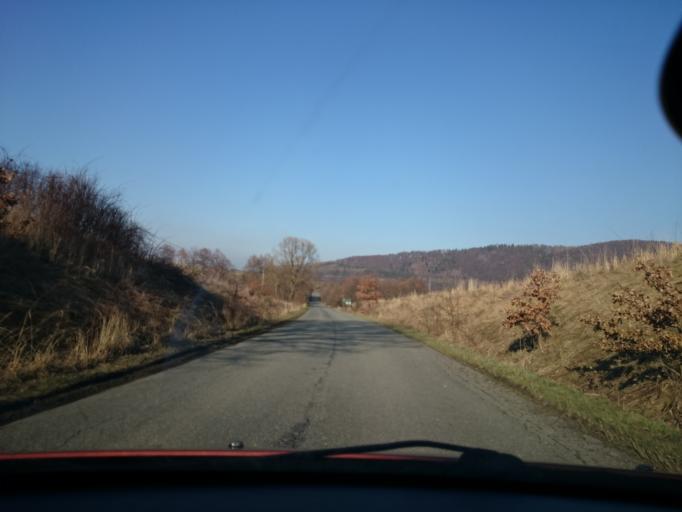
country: PL
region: Lower Silesian Voivodeship
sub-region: Powiat klodzki
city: Bystrzyca Klodzka
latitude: 50.3578
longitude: 16.6293
